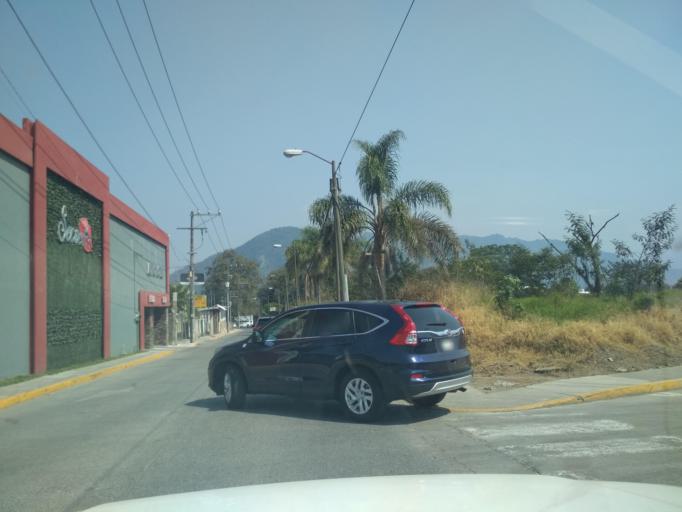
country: MX
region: Veracruz
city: Orizaba
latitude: 18.8437
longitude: -97.0876
